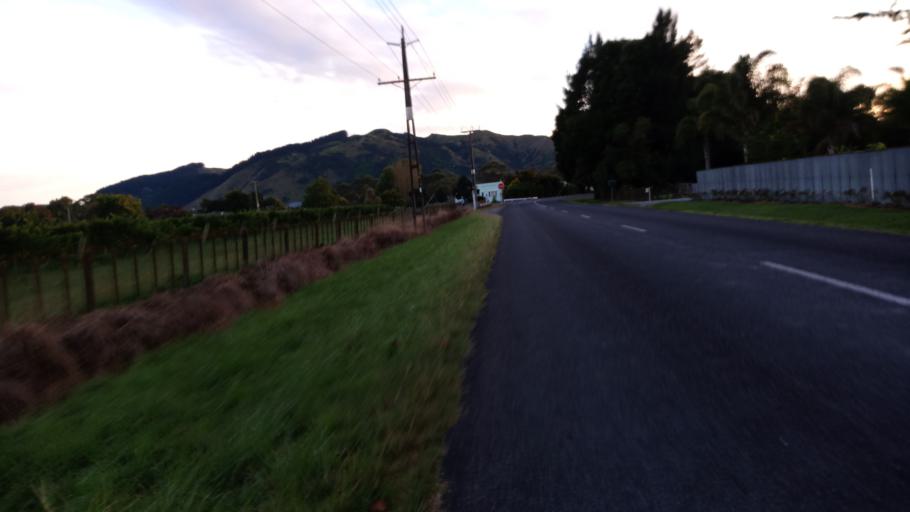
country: NZ
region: Gisborne
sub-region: Gisborne District
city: Gisborne
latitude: -38.6211
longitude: 177.9803
